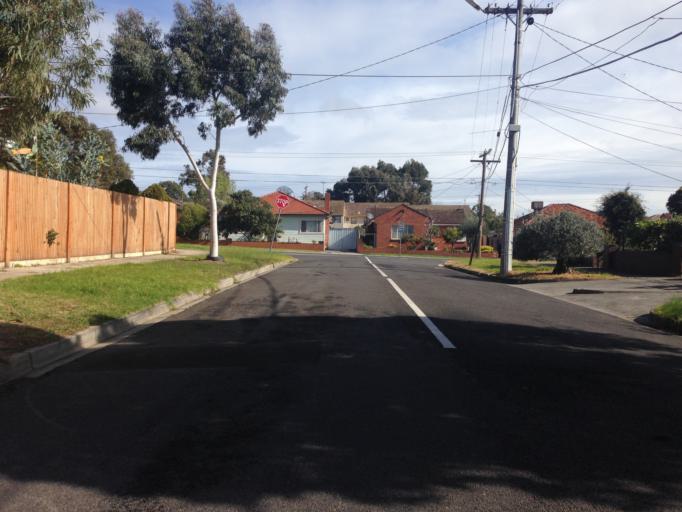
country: AU
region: Victoria
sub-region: Darebin
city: Preston
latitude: -37.7573
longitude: 145.0231
